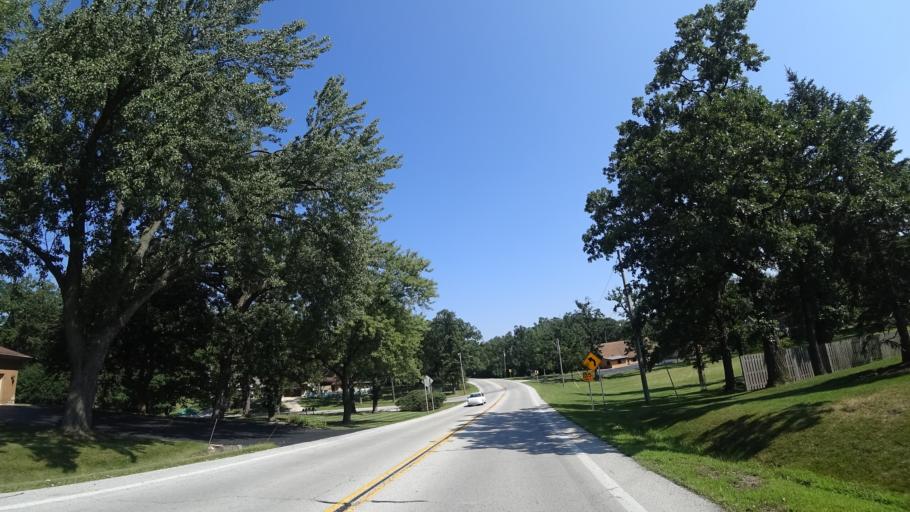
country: US
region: Illinois
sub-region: Cook County
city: Oak Forest
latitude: 41.5798
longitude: -87.7556
